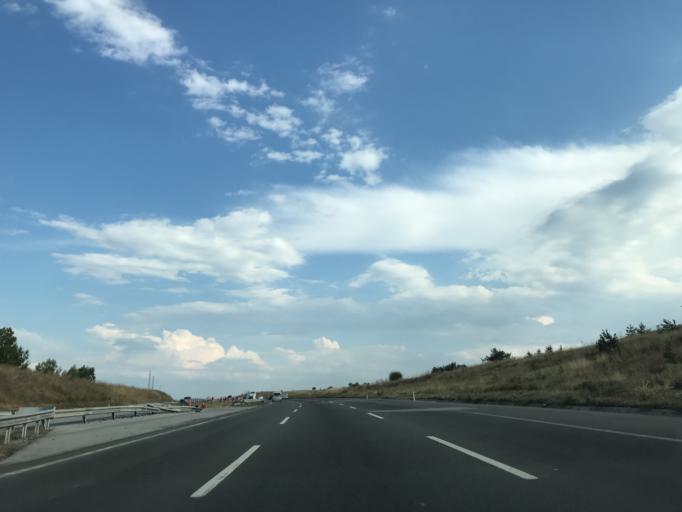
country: TR
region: Bolu
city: Yenicaga
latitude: 40.7588
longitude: 32.0632
